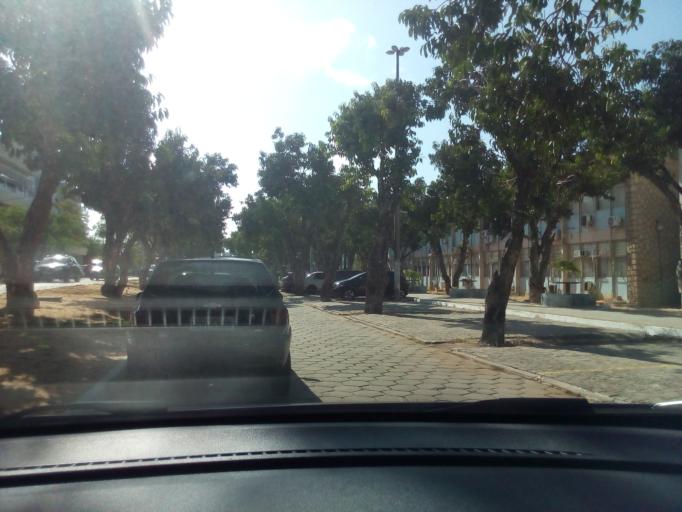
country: BR
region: Rio Grande do Norte
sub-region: Natal
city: Natal
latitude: -5.8398
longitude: -35.1977
